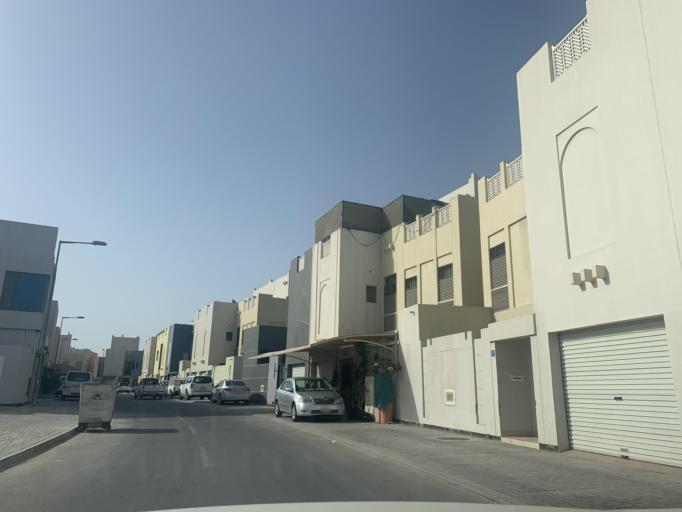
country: BH
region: Northern
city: Sitrah
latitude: 26.1632
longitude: 50.6285
